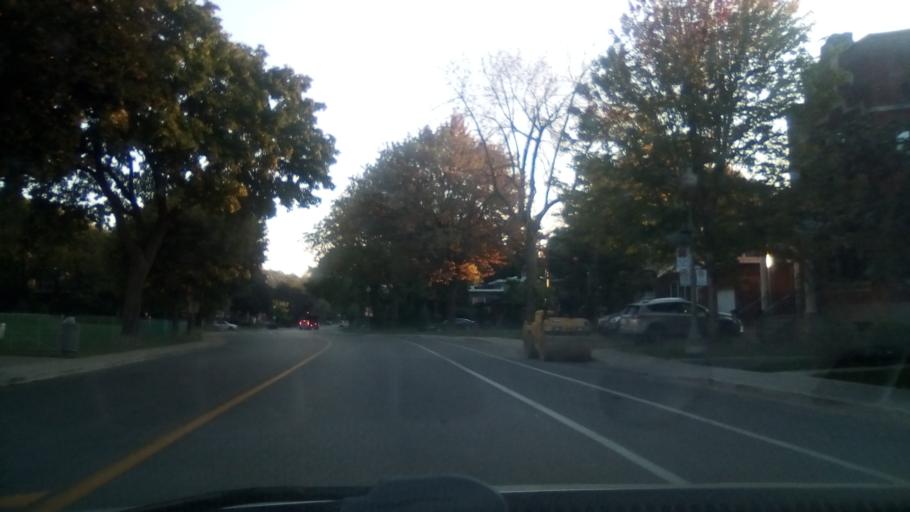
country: CA
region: Quebec
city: Westmount
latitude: 45.4807
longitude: -73.6108
